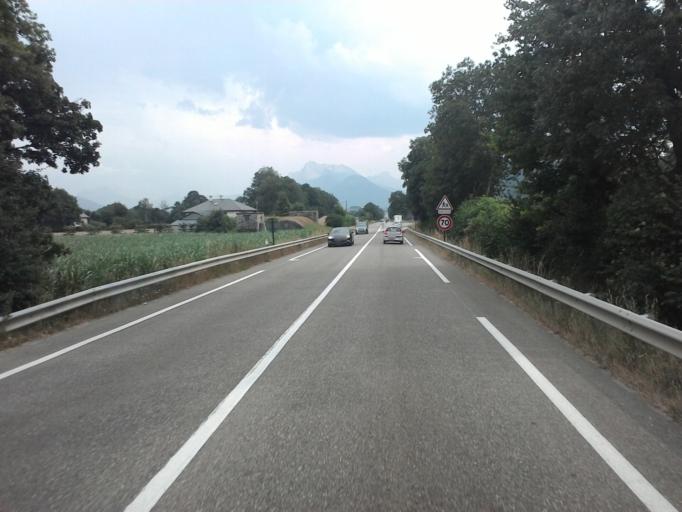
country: FR
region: Rhone-Alpes
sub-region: Departement de l'Isere
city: Pierre-Chatel
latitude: 44.9450
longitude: 5.7797
